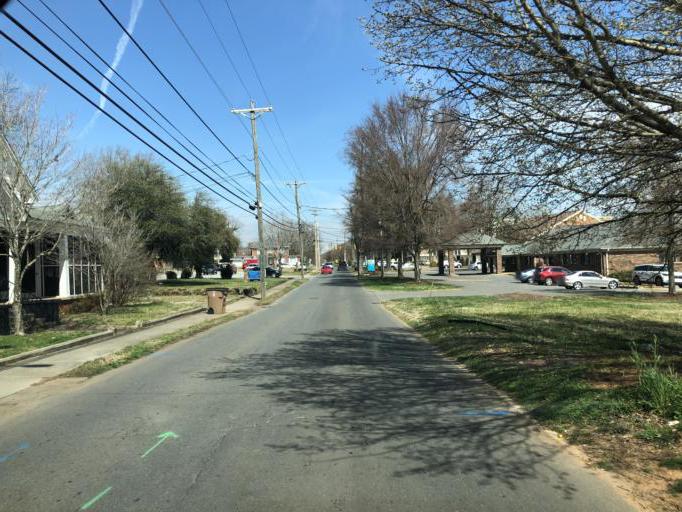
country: US
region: North Carolina
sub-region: Cleveland County
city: Shelby
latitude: 35.2999
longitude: -81.5380
